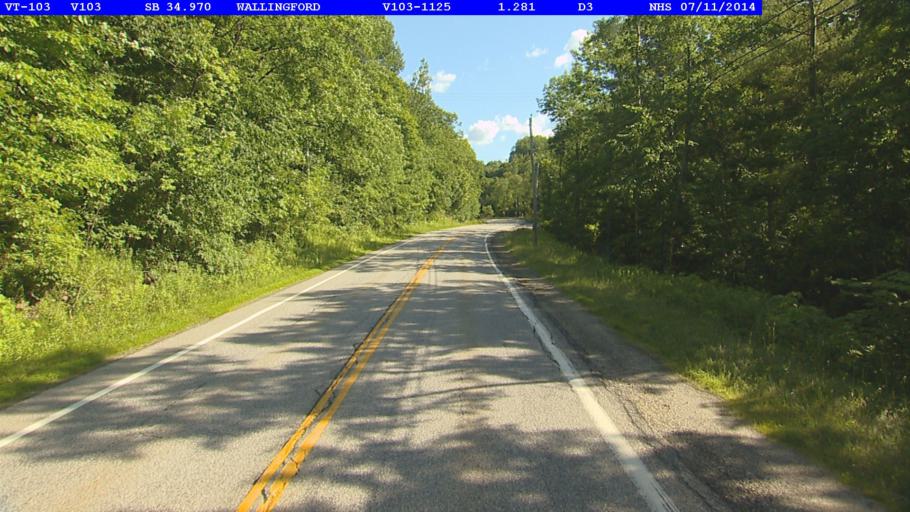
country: US
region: Vermont
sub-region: Rutland County
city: Rutland
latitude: 43.4683
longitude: -72.8749
